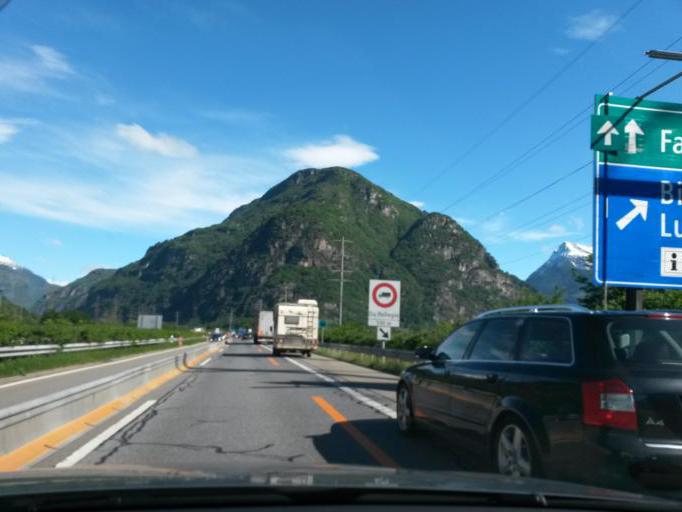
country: CH
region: Ticino
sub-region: Riviera District
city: Biasca
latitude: 46.3477
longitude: 8.9650
